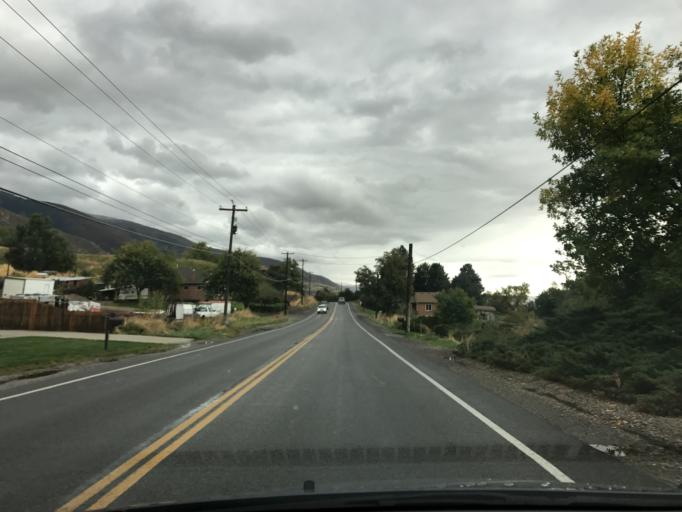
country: US
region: Utah
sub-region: Davis County
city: Farmington
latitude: 40.9981
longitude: -111.8982
